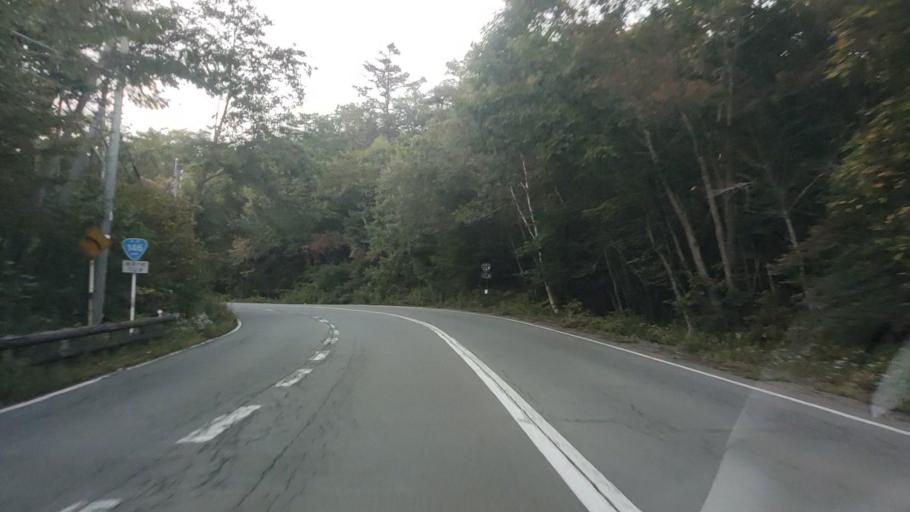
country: JP
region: Nagano
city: Komoro
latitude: 36.3945
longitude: 138.5834
